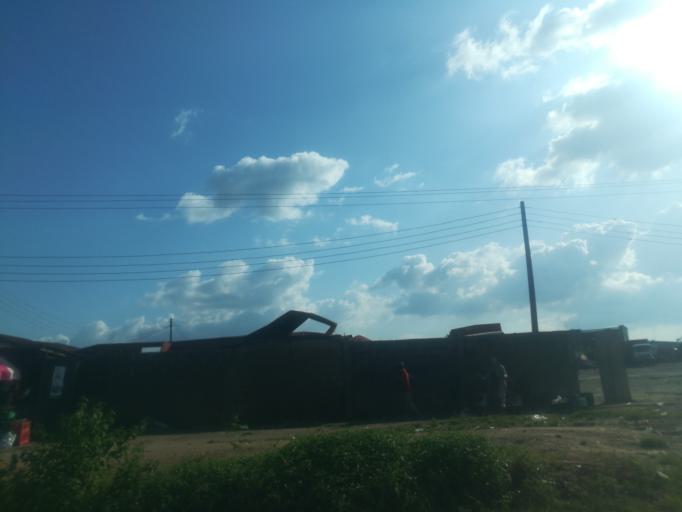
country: NG
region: Oyo
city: Egbeda
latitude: 7.3854
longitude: 3.9843
